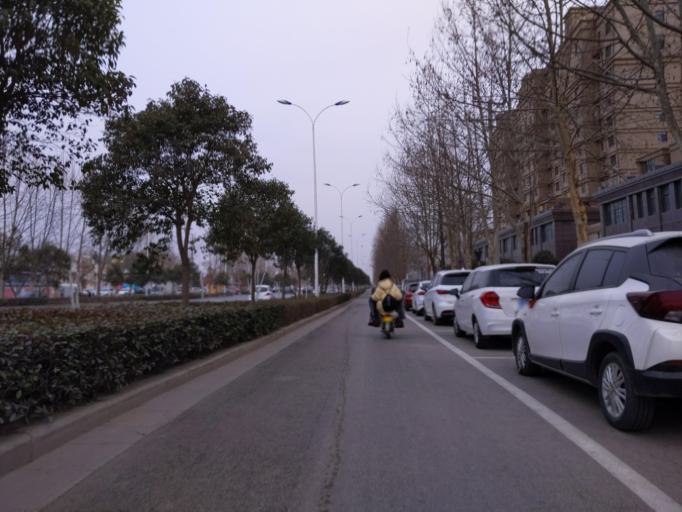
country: CN
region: Henan Sheng
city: Zhongyuanlu
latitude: 35.7562
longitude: 115.0834
